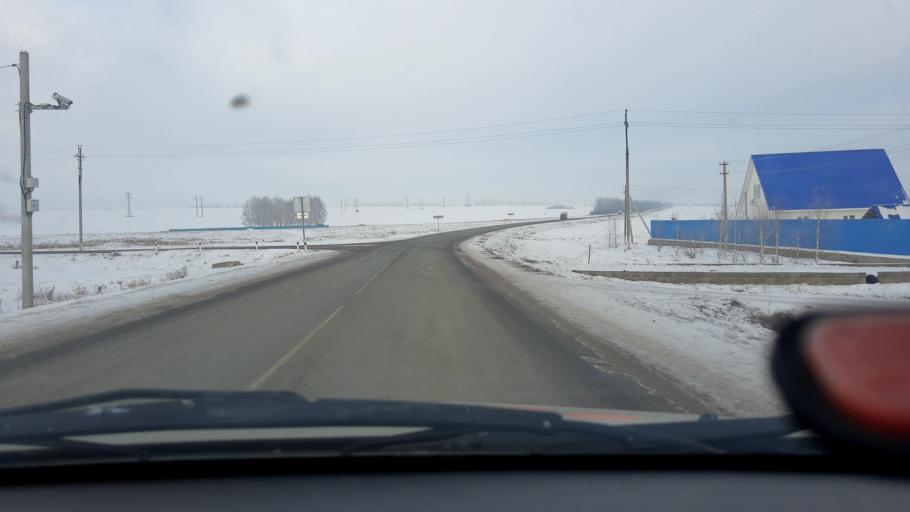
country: RU
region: Bashkortostan
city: Avdon
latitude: 54.3829
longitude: 55.8064
